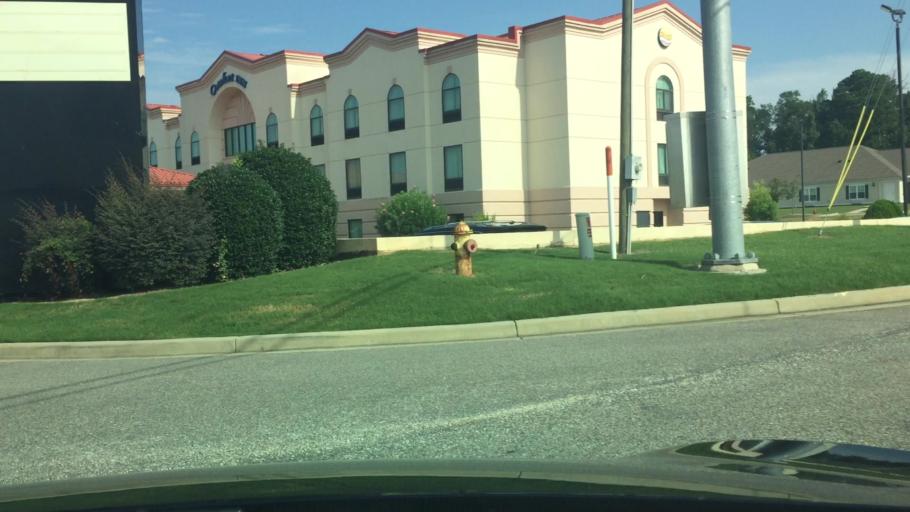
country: US
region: Alabama
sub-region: Butler County
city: Greenville
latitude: 31.8541
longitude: -86.6412
